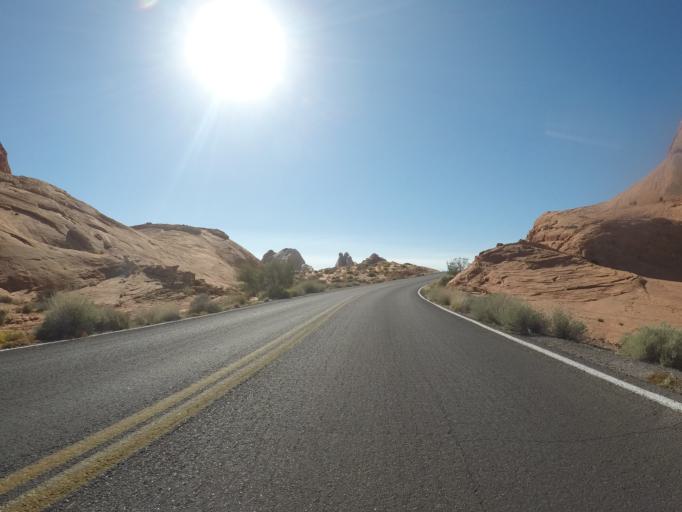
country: US
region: Nevada
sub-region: Clark County
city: Moapa Valley
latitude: 36.4919
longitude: -114.5334
